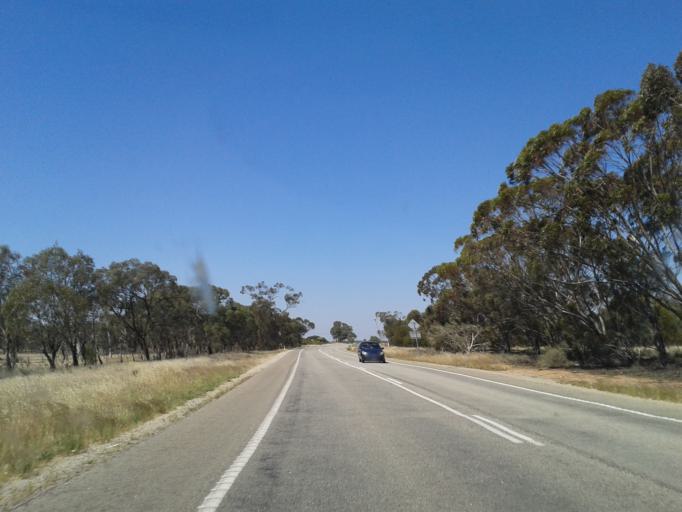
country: AU
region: Victoria
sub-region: Swan Hill
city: Swan Hill
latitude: -35.2097
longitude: 143.4068
